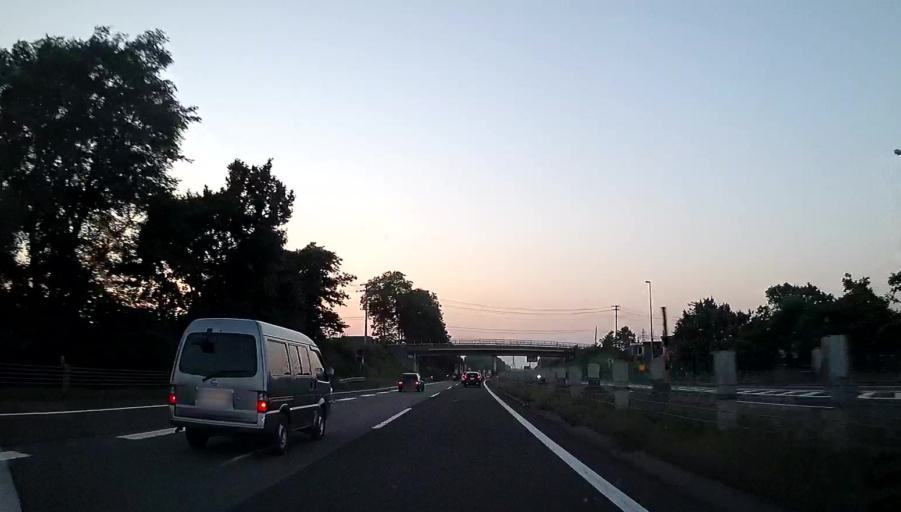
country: JP
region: Hokkaido
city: Kitahiroshima
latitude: 42.9789
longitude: 141.4760
